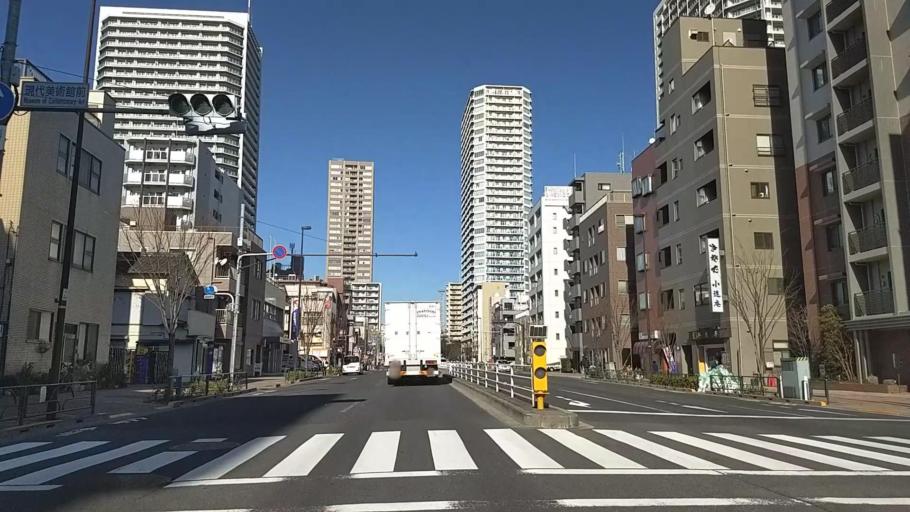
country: JP
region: Tokyo
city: Urayasu
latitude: 35.6803
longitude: 139.8067
